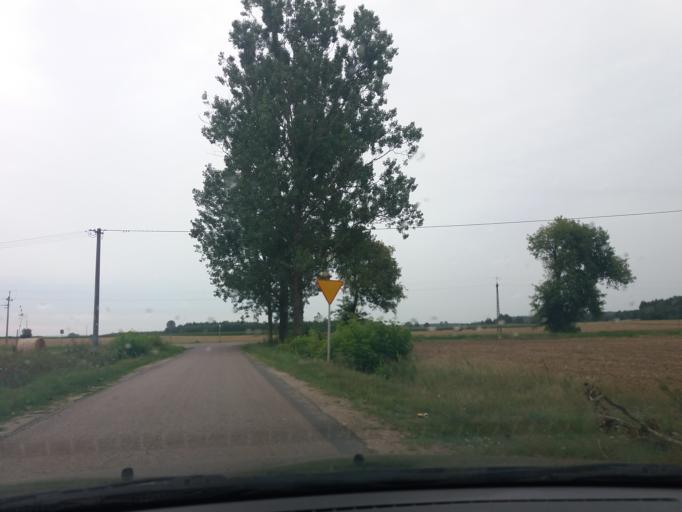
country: PL
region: Masovian Voivodeship
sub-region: Powiat mlawski
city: Wieczfnia Koscielna
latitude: 53.2166
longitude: 20.5094
